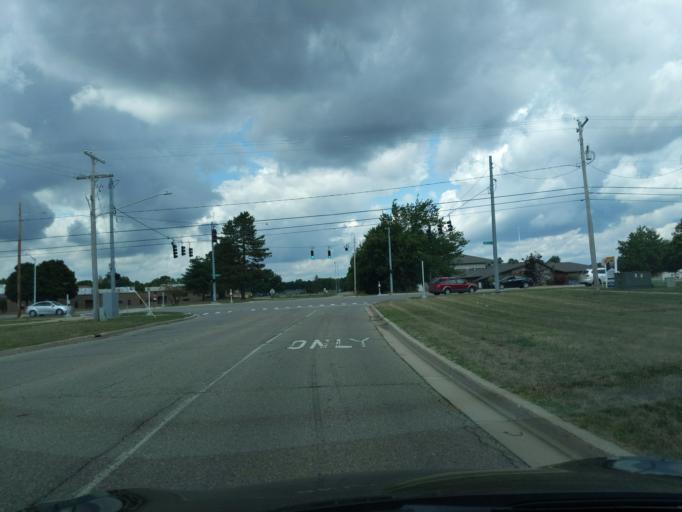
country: US
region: Michigan
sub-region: Ingham County
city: Holt
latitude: 42.6397
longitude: -84.5727
